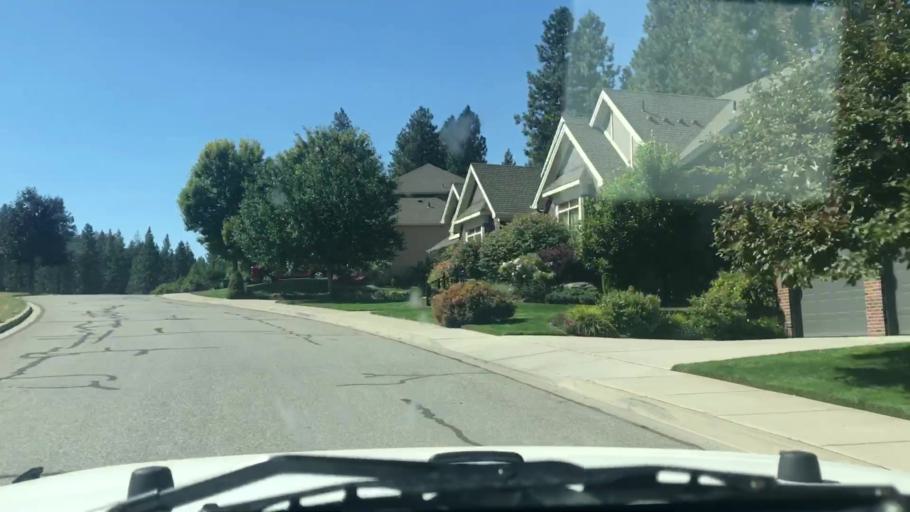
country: US
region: Washington
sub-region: Spokane County
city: Spokane
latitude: 47.5952
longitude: -117.4194
